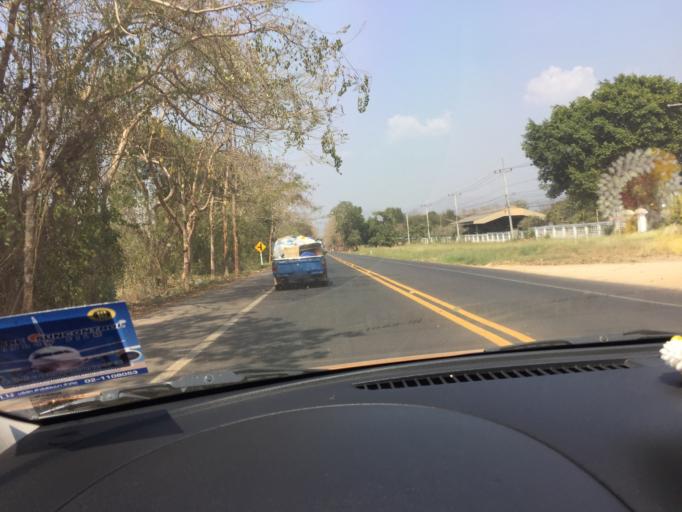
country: TH
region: Kanchanaburi
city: Sai Yok
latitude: 14.1737
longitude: 99.1293
